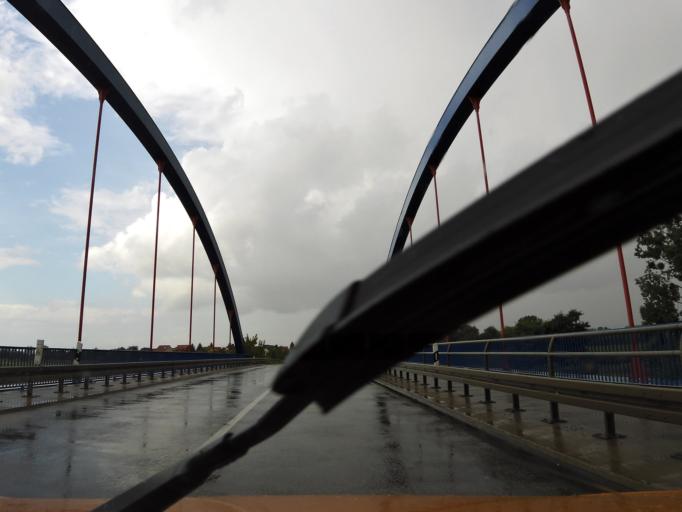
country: DE
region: Brandenburg
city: Wustermark
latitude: 52.4884
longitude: 12.9305
